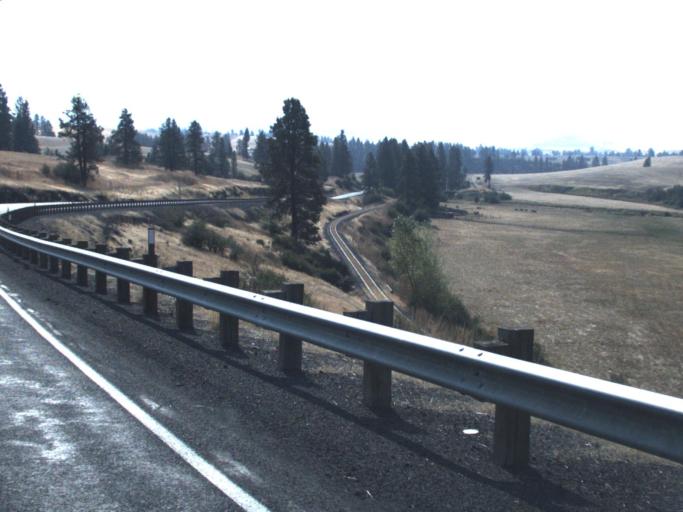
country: US
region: Washington
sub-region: Whitman County
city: Pullman
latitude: 46.9378
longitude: -117.0988
